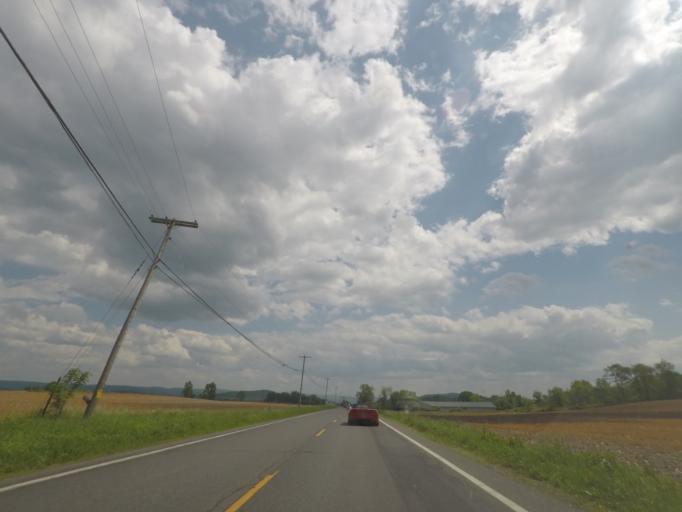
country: US
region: New York
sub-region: Dutchess County
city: Pine Plains
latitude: 41.8925
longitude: -73.5311
